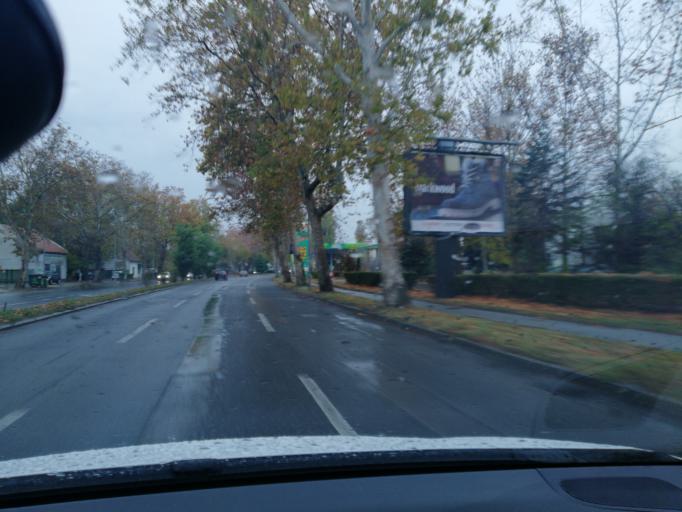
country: RS
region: Autonomna Pokrajina Vojvodina
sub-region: Juznobacki Okrug
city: Novi Sad
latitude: 45.2484
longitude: 19.8149
